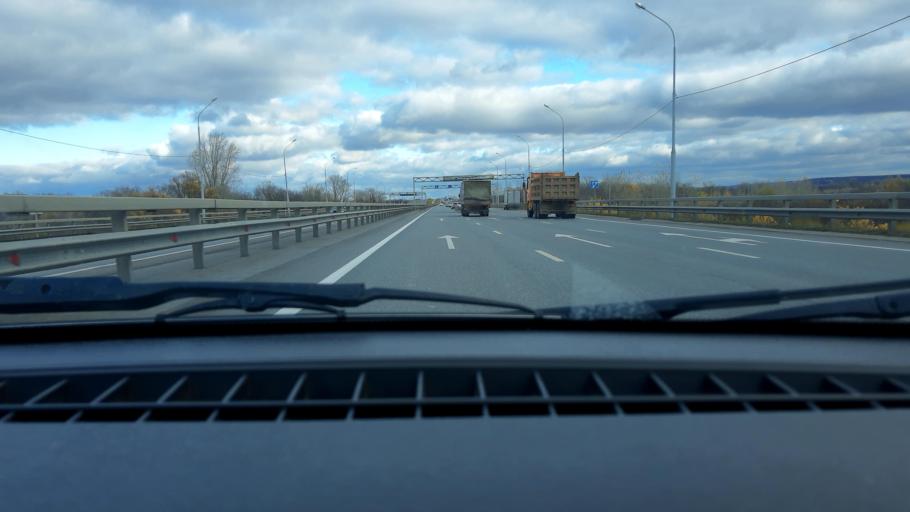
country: RU
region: Bashkortostan
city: Ufa
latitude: 54.6447
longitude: 55.9842
